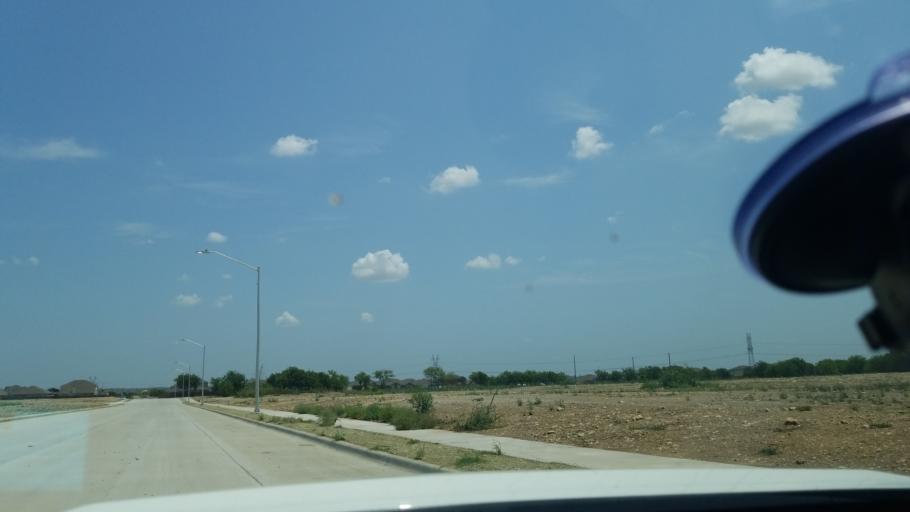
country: US
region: Texas
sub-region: Tarrant County
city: Saginaw
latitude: 32.9138
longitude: -97.3716
